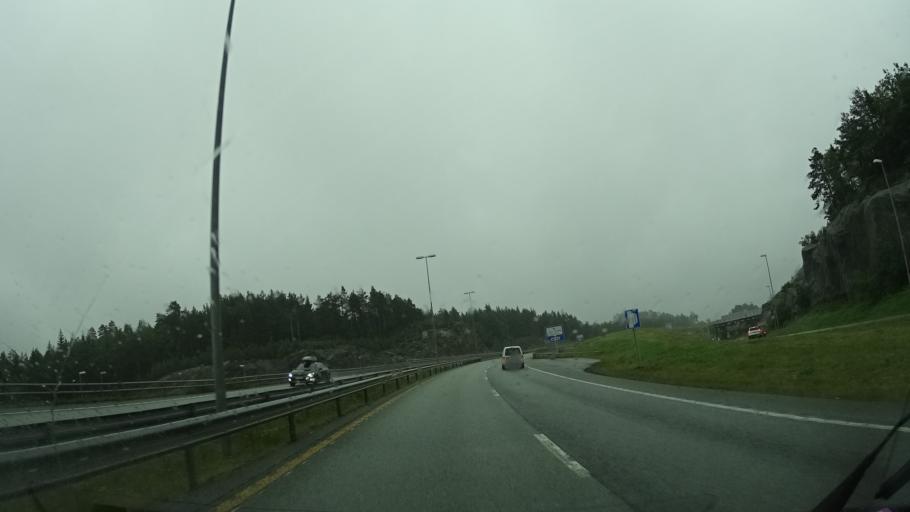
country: NO
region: Vest-Agder
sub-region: Kristiansand
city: Tveit
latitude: 58.1812
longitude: 8.1193
